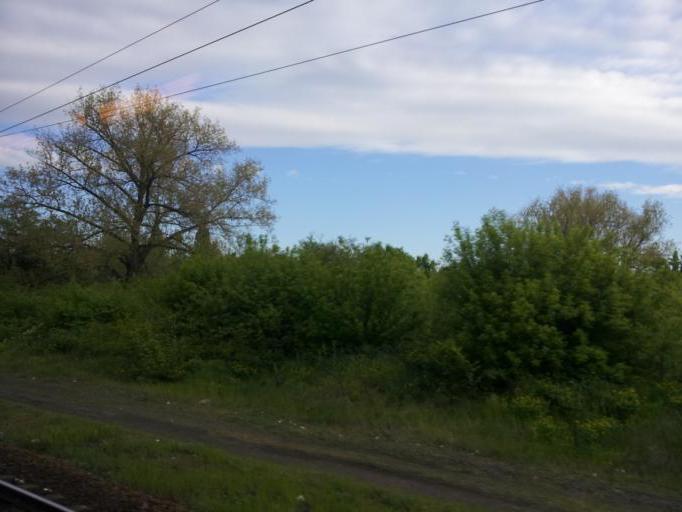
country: HU
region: Budapest
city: Budapest XIII. keruelet
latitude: 47.5213
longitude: 19.0870
